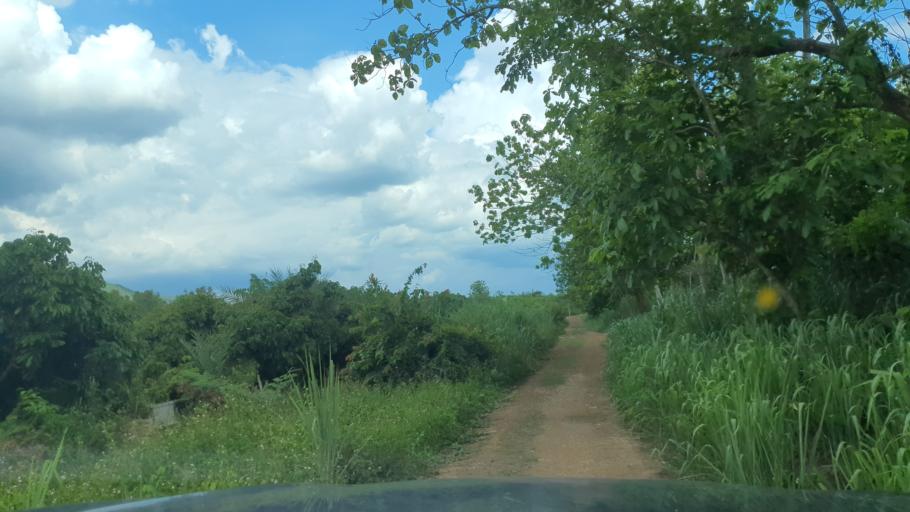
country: TH
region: Chiang Mai
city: Mae Taeng
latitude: 19.1250
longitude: 99.0514
